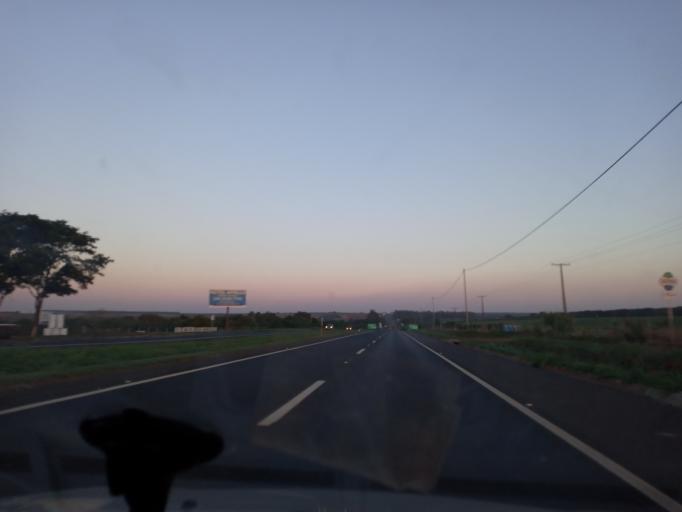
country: BR
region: Minas Gerais
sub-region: Uberlandia
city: Uberlandia
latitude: -18.8865
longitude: -48.4601
